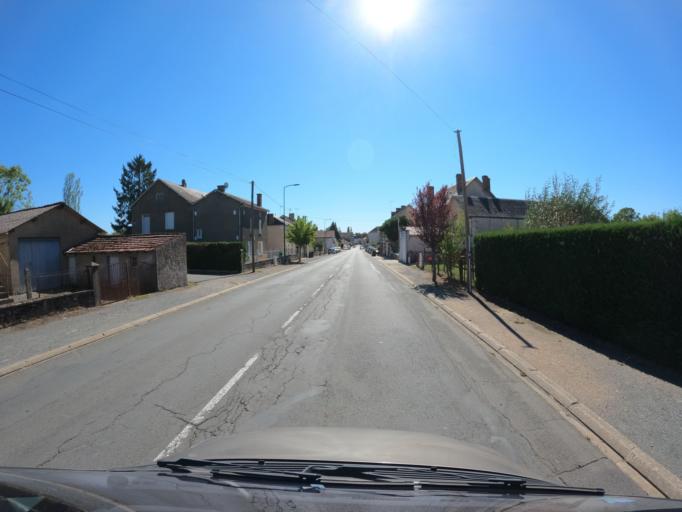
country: FR
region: Poitou-Charentes
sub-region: Departement de la Vienne
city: Lathus-Saint-Remy
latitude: 46.3363
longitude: 0.9566
